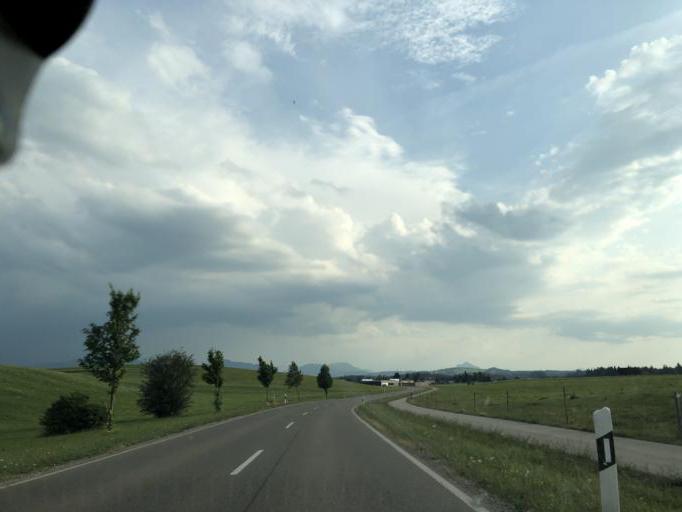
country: DE
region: Bavaria
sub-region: Swabia
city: Gorisried
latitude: 47.7151
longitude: 10.5100
